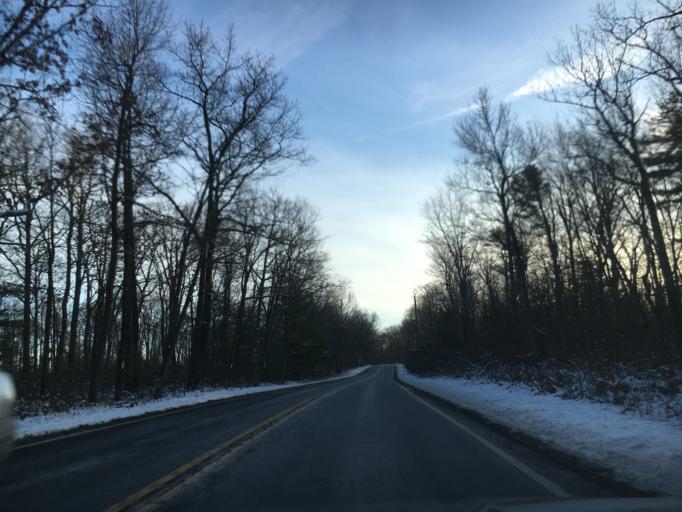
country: US
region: Pennsylvania
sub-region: Pike County
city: Hemlock Farms
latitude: 41.3598
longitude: -75.1284
